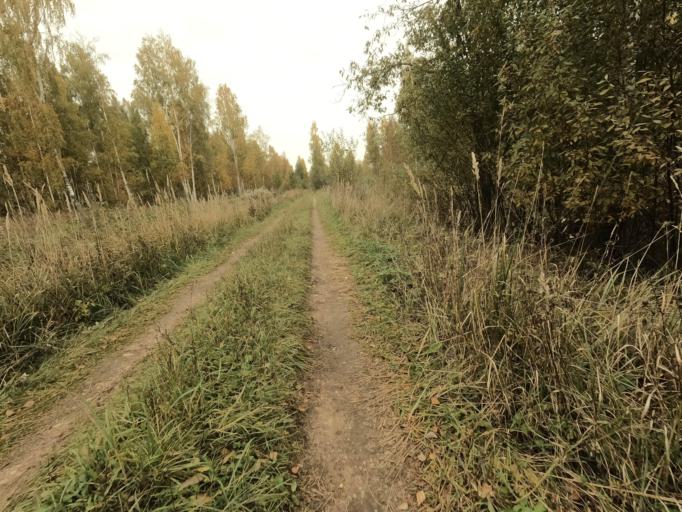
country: RU
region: Novgorod
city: Pankovka
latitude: 58.8752
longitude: 30.9396
